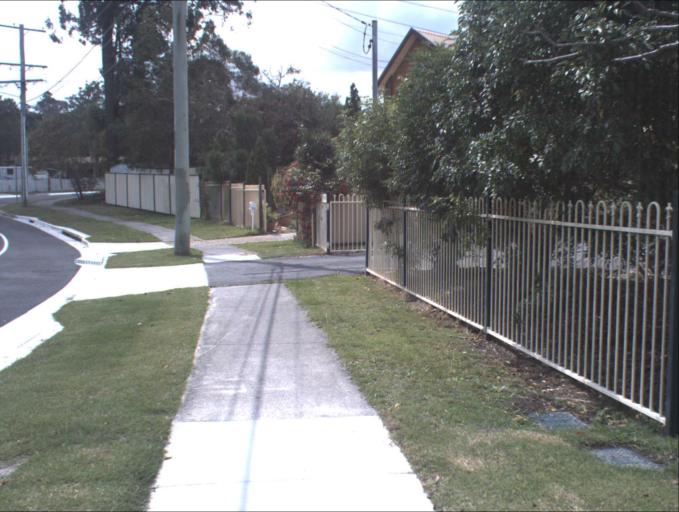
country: AU
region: Queensland
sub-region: Brisbane
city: Sunnybank Hills
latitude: -27.6599
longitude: 153.0524
